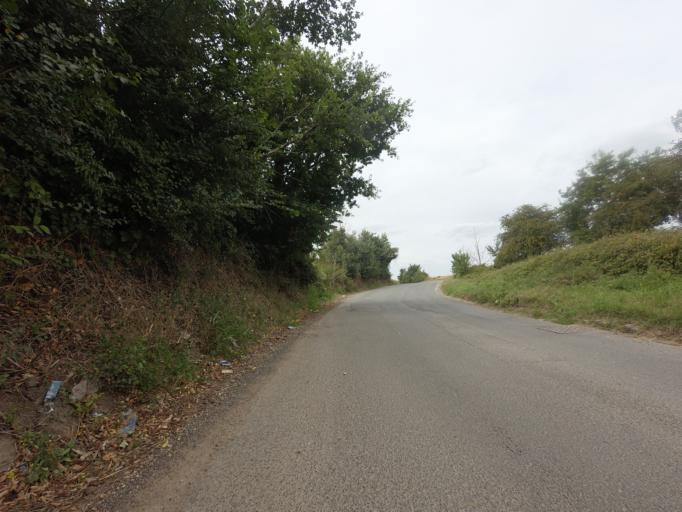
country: GB
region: England
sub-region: Medway
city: Stoke
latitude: 51.4395
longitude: 0.6027
